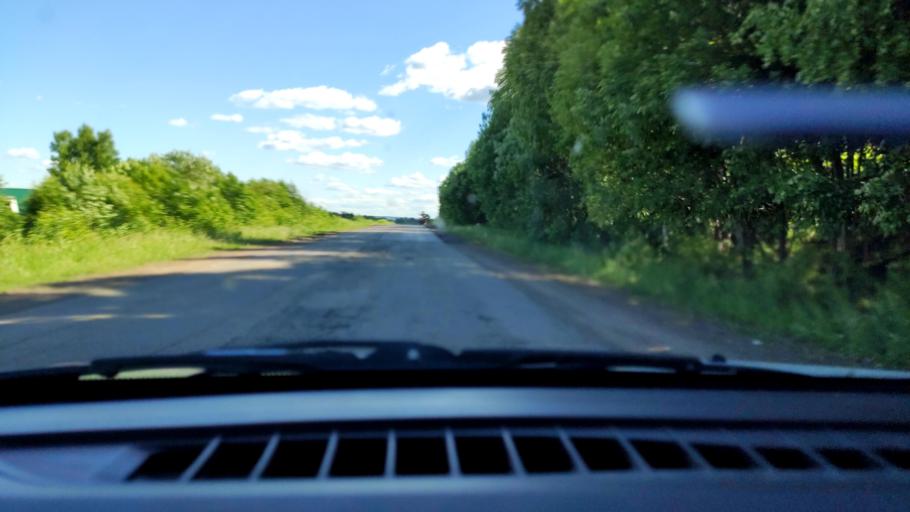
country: RU
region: Perm
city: Uinskoye
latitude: 57.1741
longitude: 56.5615
